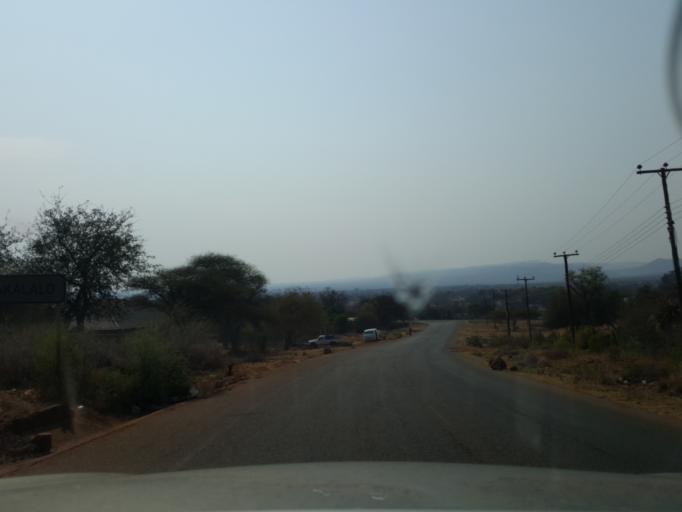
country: BW
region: South East
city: Lobatse
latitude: -25.2856
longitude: 25.8949
